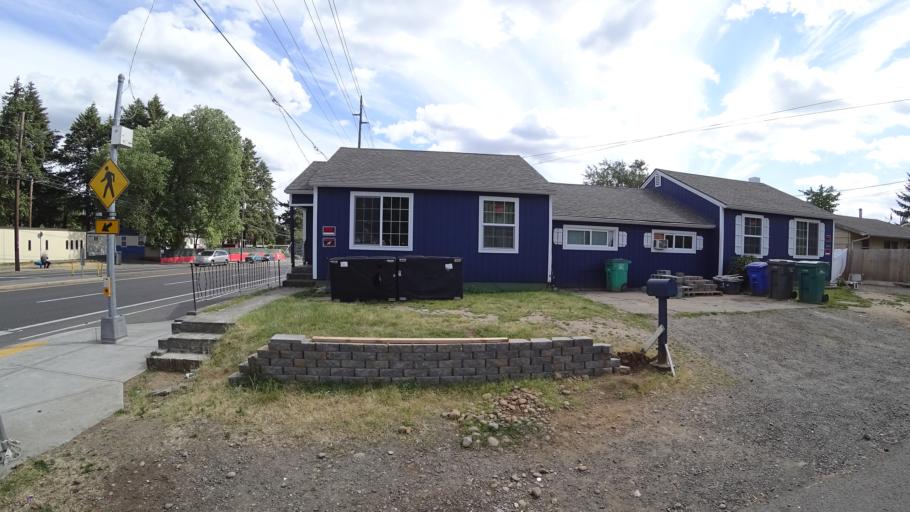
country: US
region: Oregon
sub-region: Multnomah County
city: Lents
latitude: 45.4920
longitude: -122.5379
